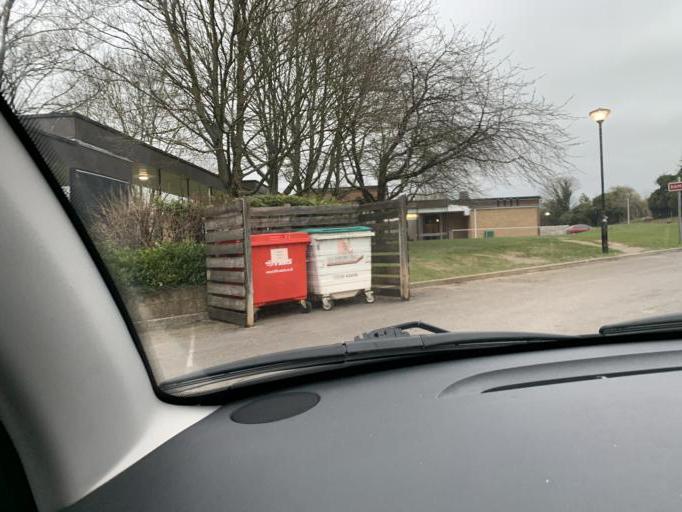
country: GB
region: England
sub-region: Wiltshire
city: Amesbury
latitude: 51.1732
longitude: -1.7741
